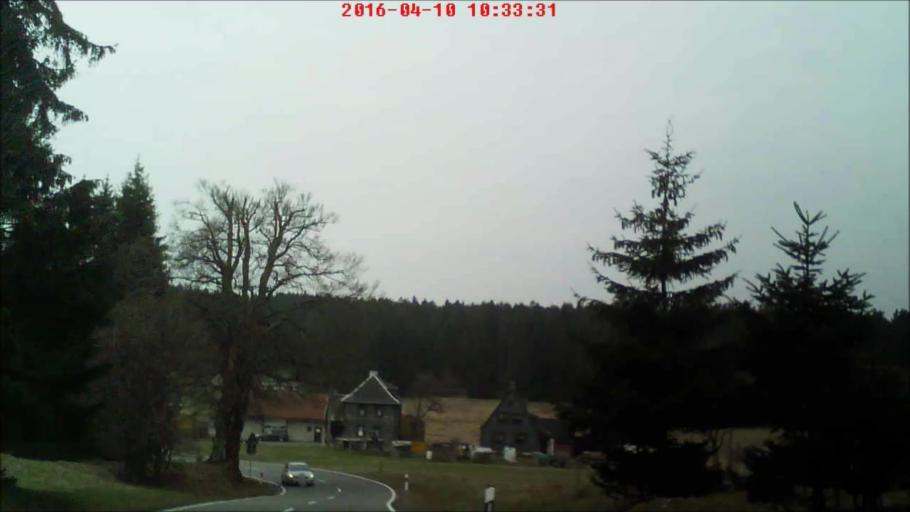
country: DE
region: Thuringia
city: Stutzerbach
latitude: 50.6069
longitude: 10.8647
